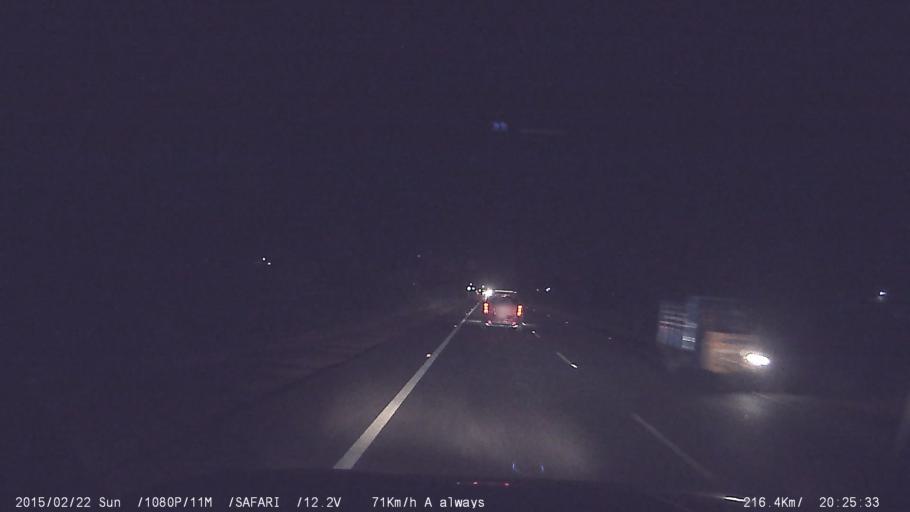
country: IN
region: Tamil Nadu
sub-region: Dindigul
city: Dindigul
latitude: 10.3161
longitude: 77.9027
